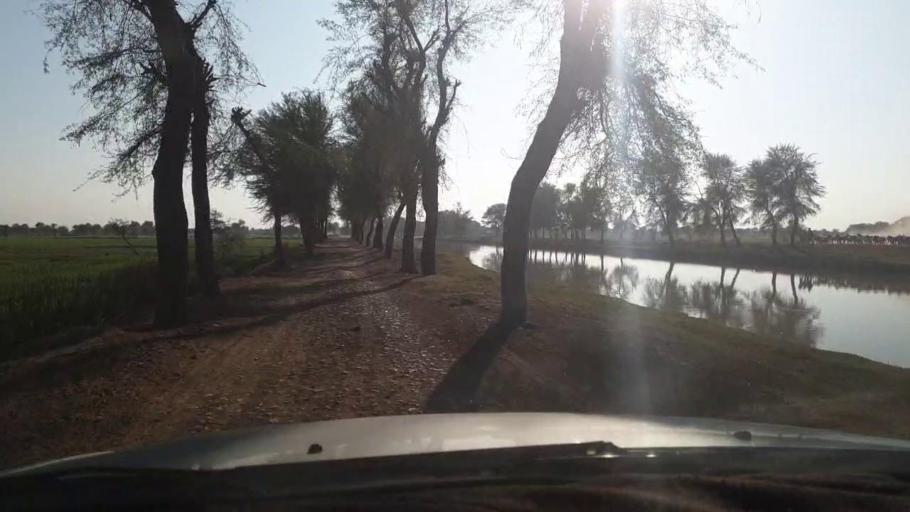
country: PK
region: Sindh
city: Mirpur Mathelo
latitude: 27.9688
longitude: 69.5232
